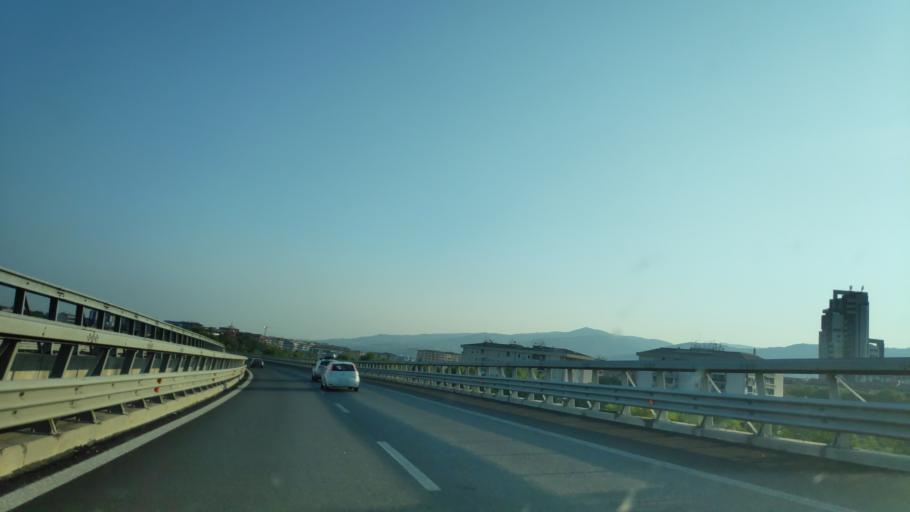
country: IT
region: Calabria
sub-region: Provincia di Cosenza
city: Cosenza
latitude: 39.3155
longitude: 16.2413
